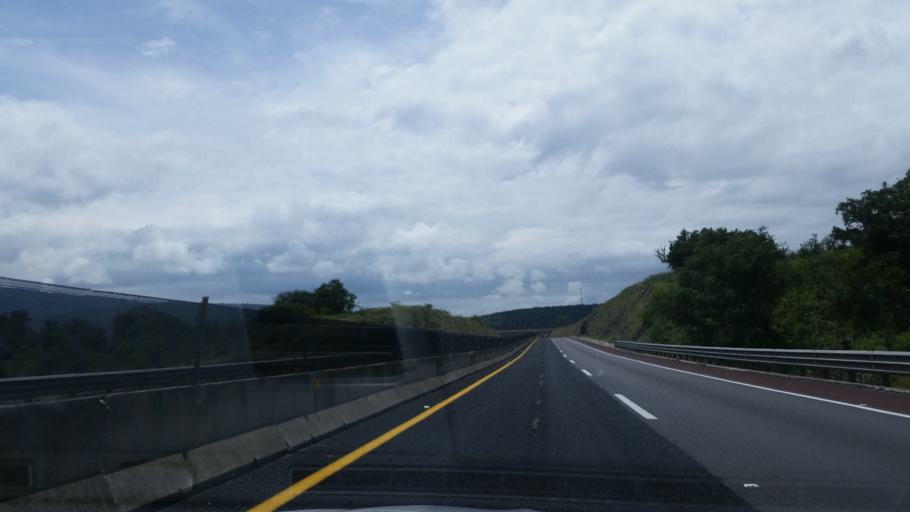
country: MX
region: Hidalgo
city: Tula de Allende
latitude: 20.0638
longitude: -99.3854
